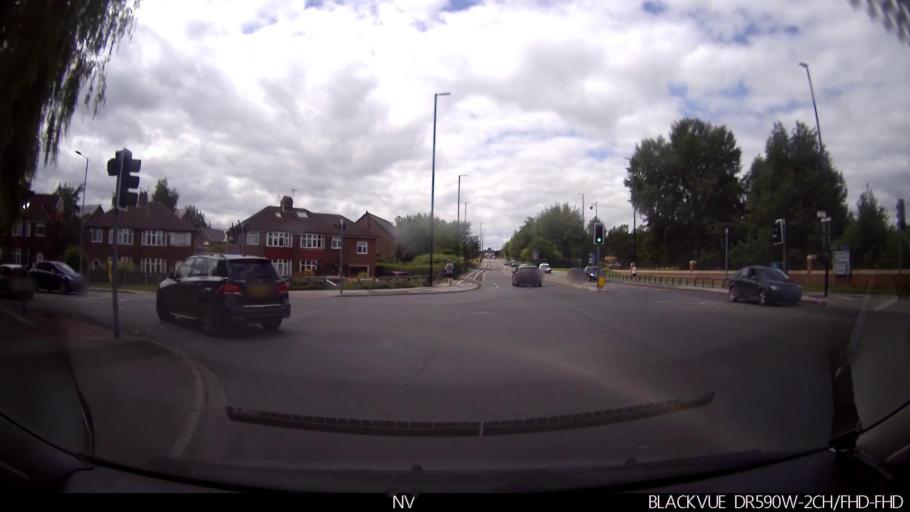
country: GB
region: England
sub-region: City of York
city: York
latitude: 53.9657
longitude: -1.1107
